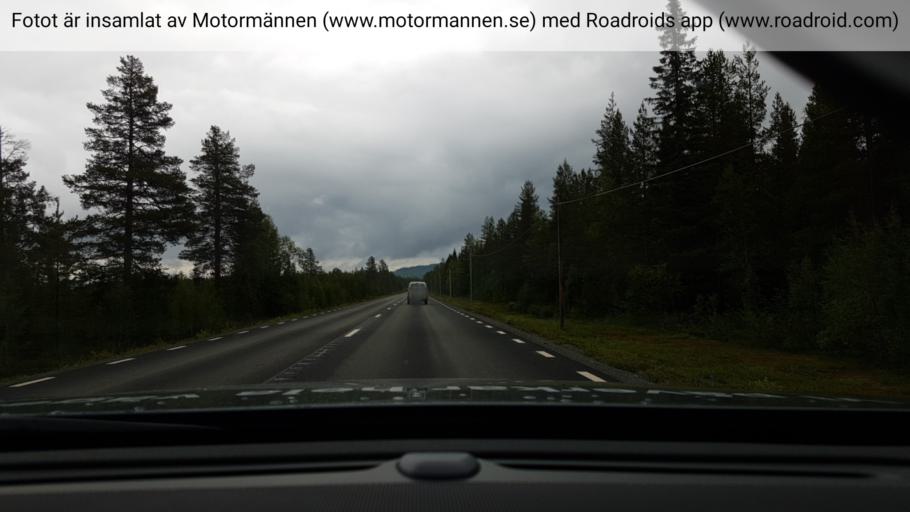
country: SE
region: Vaesterbotten
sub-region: Norsjo Kommun
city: Norsjoe
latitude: 65.2932
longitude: 19.5694
